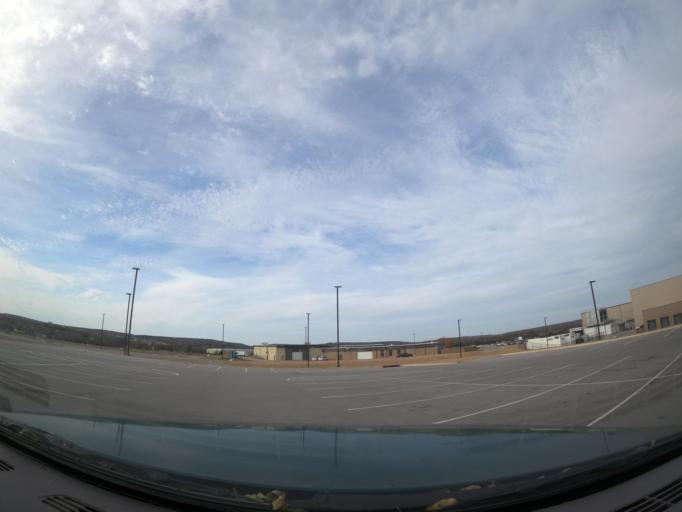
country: US
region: Oklahoma
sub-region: Tulsa County
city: Turley
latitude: 36.2078
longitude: -96.0058
